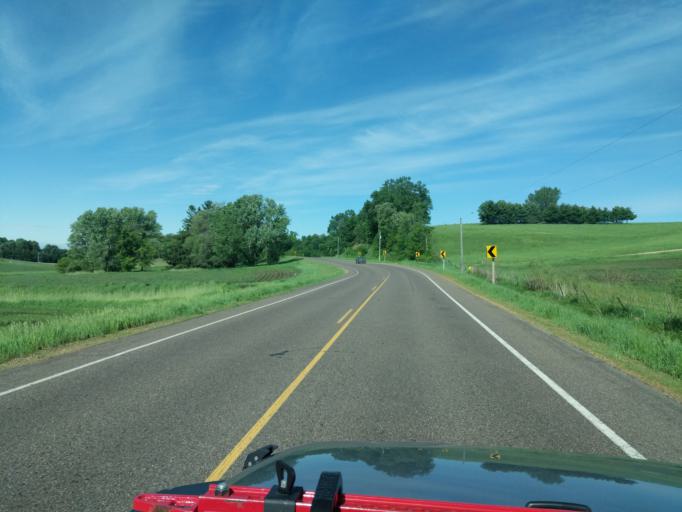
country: US
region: Wisconsin
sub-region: Pierce County
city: River Falls
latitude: 44.8699
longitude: -92.5101
